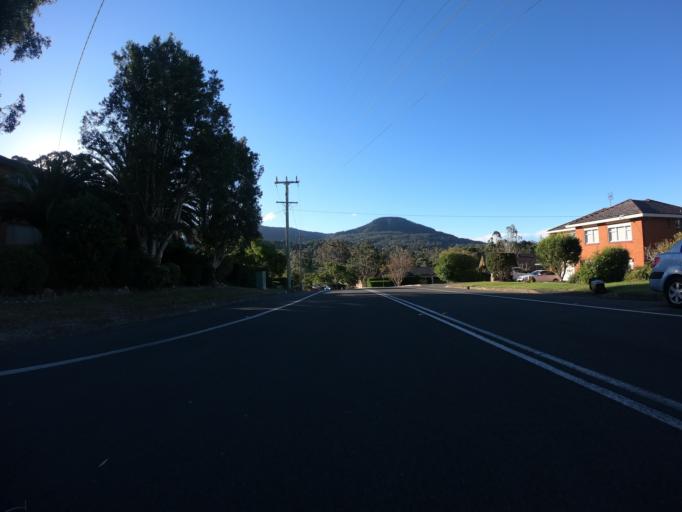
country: AU
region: New South Wales
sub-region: Wollongong
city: Mount Keira
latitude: -34.4288
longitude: 150.8477
